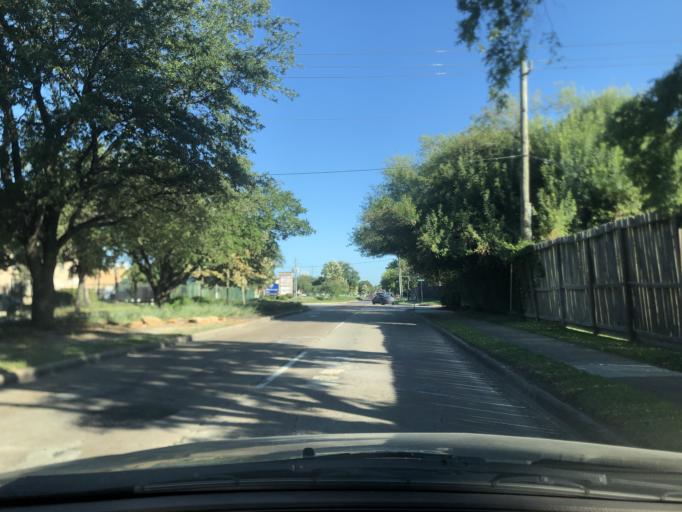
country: US
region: Texas
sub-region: Harris County
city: Bunker Hill Village
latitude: 29.7446
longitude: -95.5719
